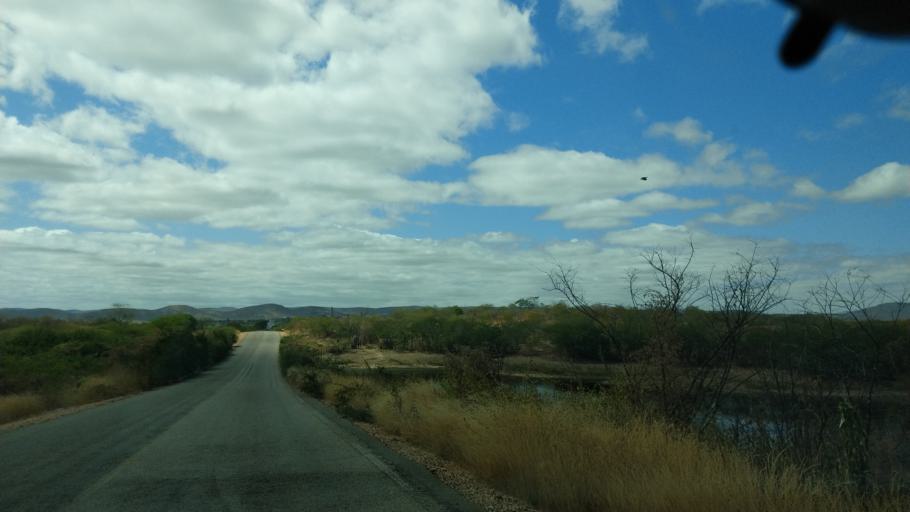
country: BR
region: Rio Grande do Norte
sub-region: Currais Novos
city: Currais Novos
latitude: -6.2704
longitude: -36.5552
